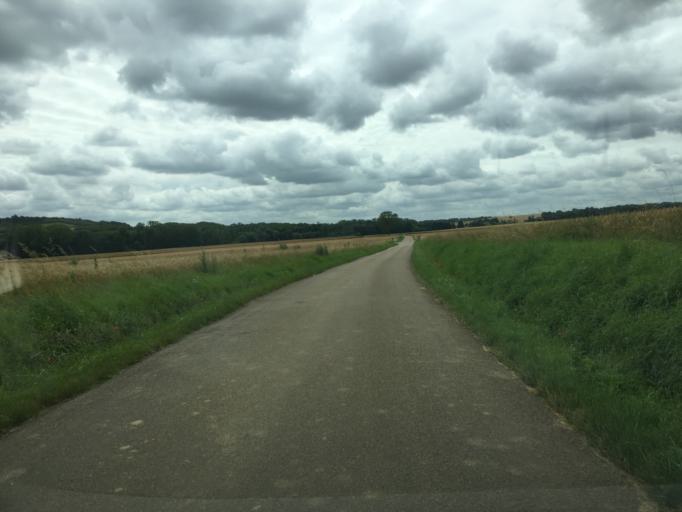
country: FR
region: Bourgogne
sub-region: Departement de l'Yonne
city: Fleury-la-Vallee
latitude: 47.8728
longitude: 3.4353
